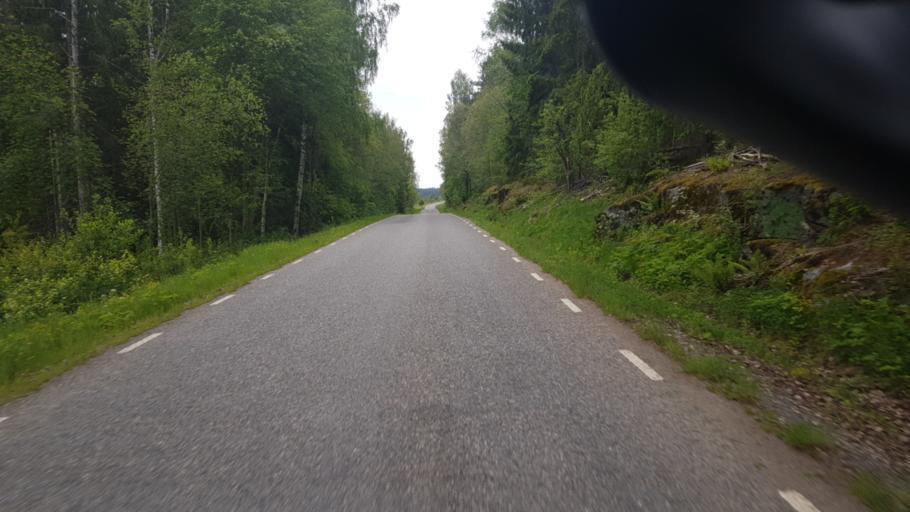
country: SE
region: Vaermland
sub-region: Eda Kommun
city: Amotfors
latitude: 59.8229
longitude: 12.4366
